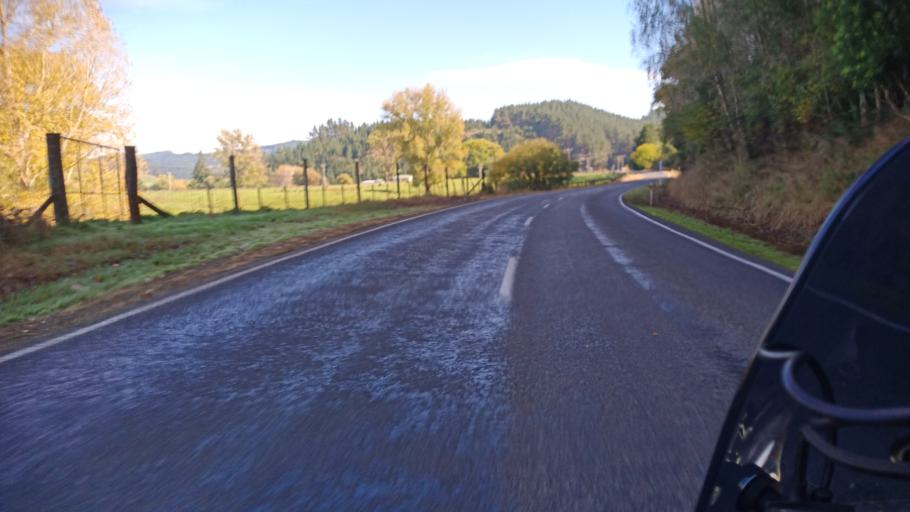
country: NZ
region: Hawke's Bay
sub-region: Wairoa District
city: Wairoa
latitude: -38.9232
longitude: 177.2700
